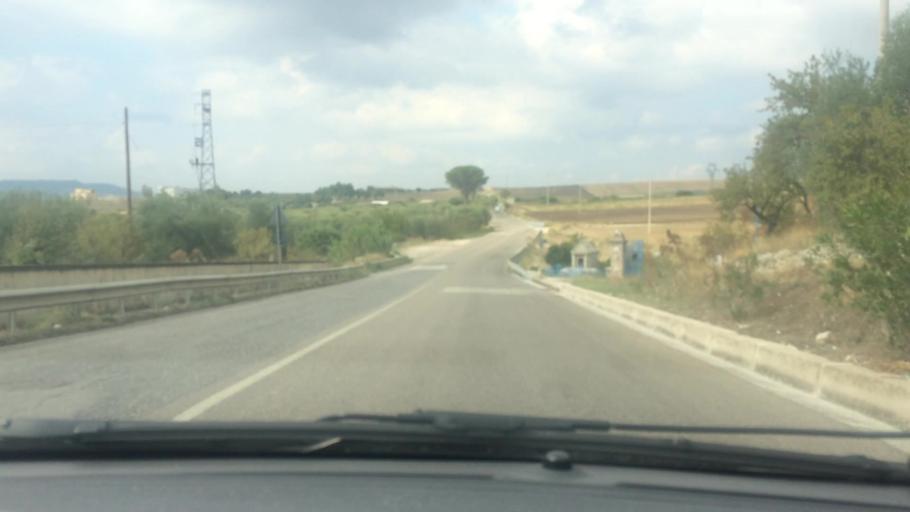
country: IT
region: Basilicate
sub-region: Provincia di Matera
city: Matera
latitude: 40.6884
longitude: 16.5647
